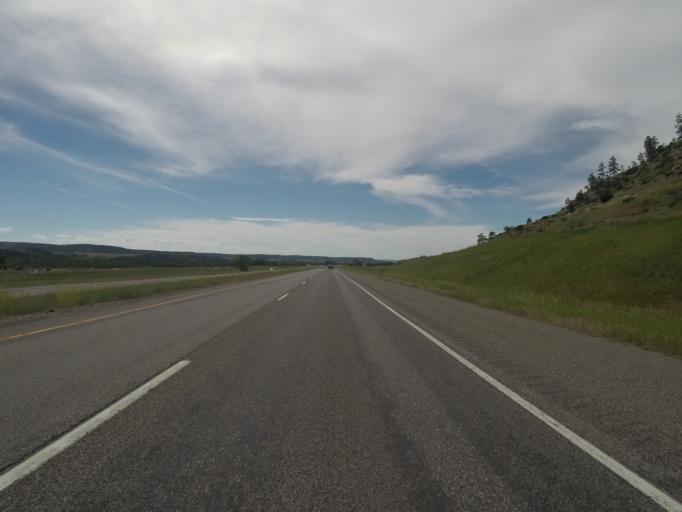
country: US
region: Montana
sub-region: Stillwater County
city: Columbus
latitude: 45.6022
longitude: -109.1402
